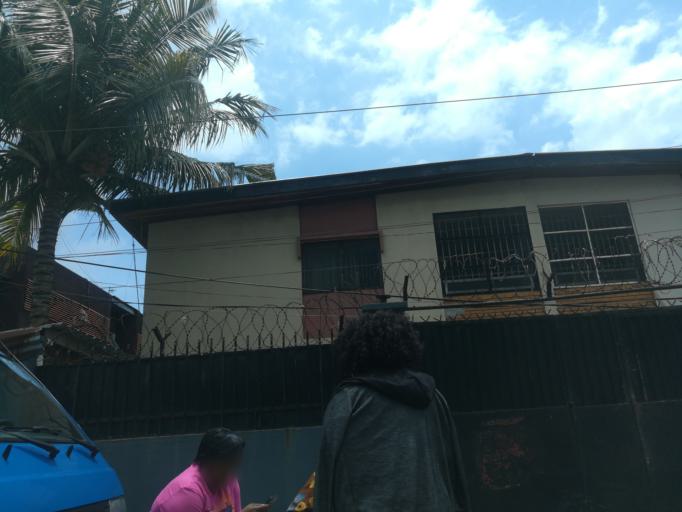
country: NG
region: Lagos
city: Somolu
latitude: 6.5530
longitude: 3.3649
